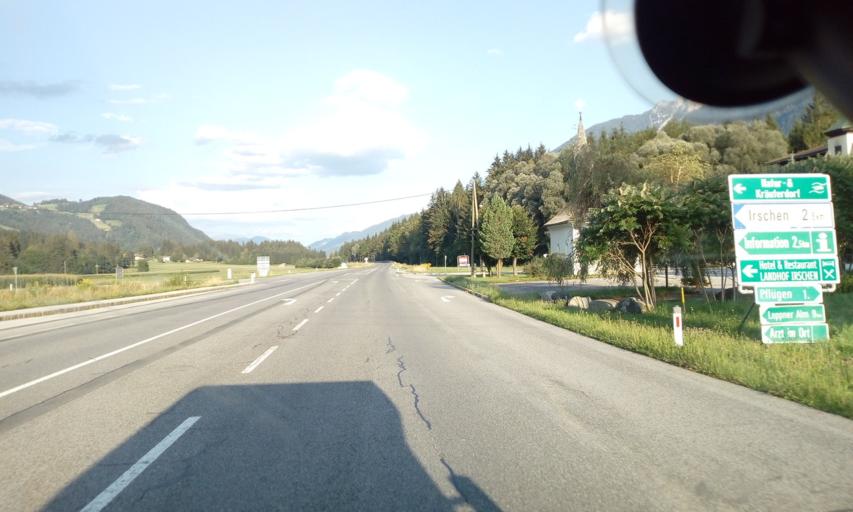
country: AT
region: Carinthia
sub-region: Politischer Bezirk Spittal an der Drau
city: Irschen
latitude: 46.7429
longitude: 13.0115
